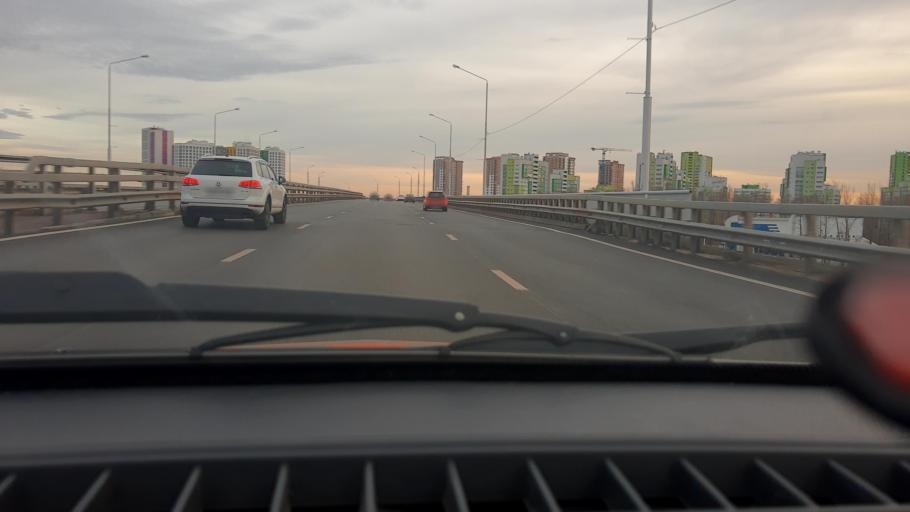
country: RU
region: Bashkortostan
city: Mikhaylovka
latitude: 54.7053
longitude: 55.8570
